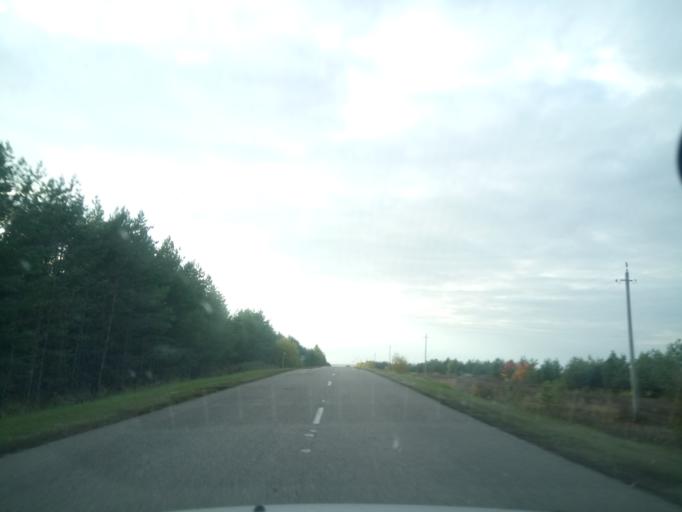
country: RU
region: Nizjnij Novgorod
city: Gagino
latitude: 55.1937
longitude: 45.1231
